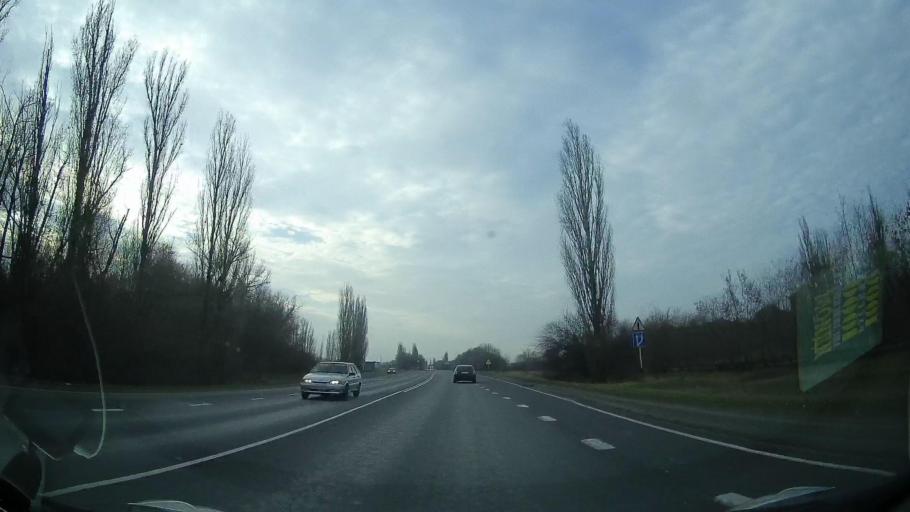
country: RU
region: Rostov
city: Ol'ginskaya
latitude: 47.1399
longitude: 40.0088
